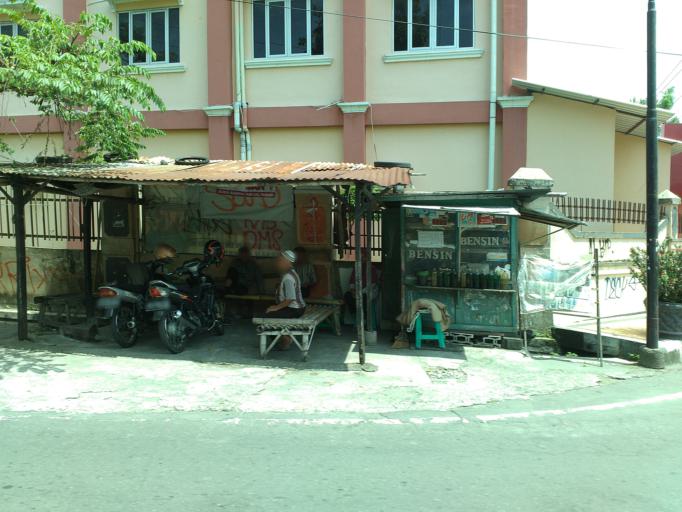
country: ID
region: Central Java
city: Klaten
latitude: -7.7085
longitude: 110.5954
